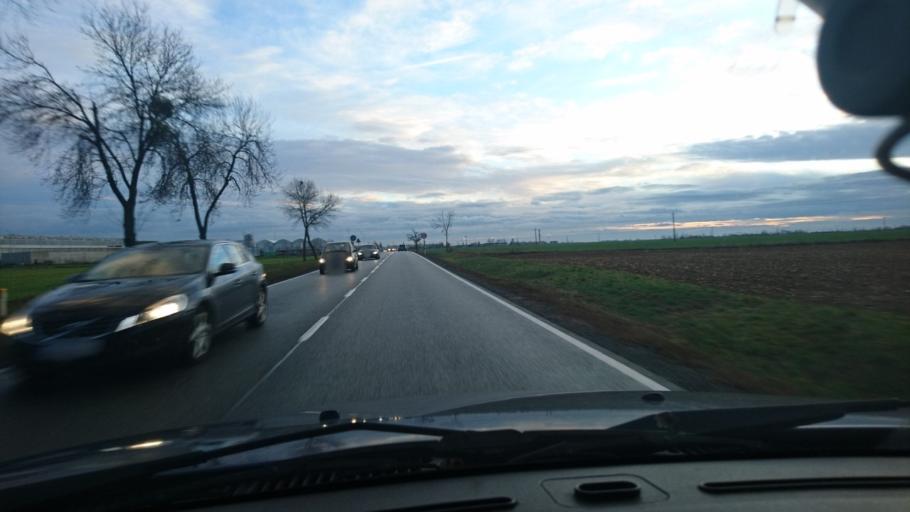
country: PL
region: Opole Voivodeship
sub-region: Powiat kluczborski
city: Kluczbork
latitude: 51.0053
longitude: 18.2048
